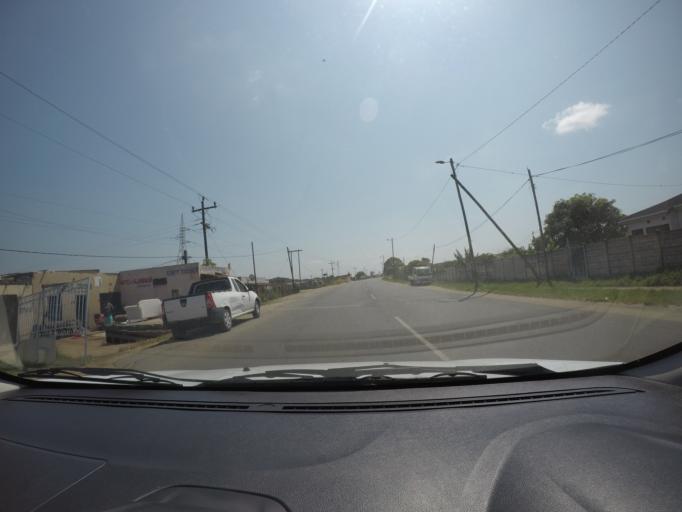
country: ZA
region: KwaZulu-Natal
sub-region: uThungulu District Municipality
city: eSikhawini
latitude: -28.8625
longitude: 31.9135
